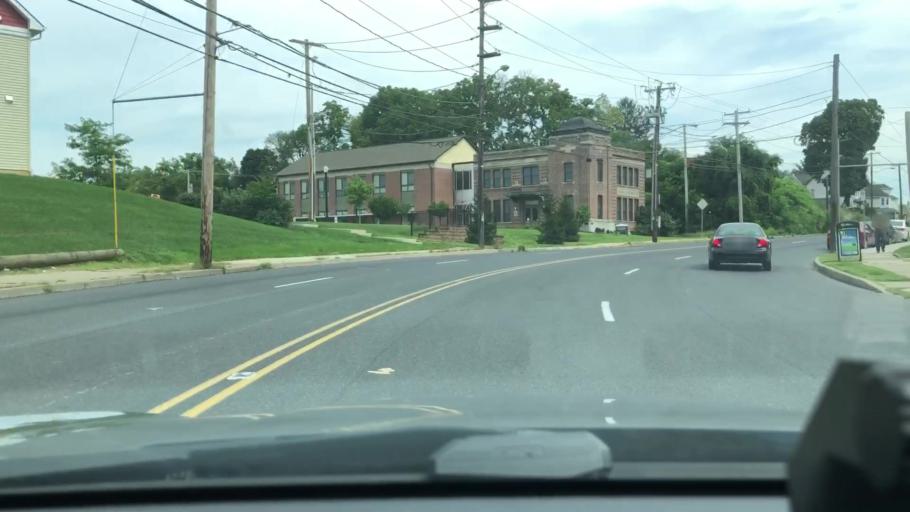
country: US
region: Pennsylvania
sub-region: Lehigh County
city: Fullerton
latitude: 40.6123
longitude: -75.4484
